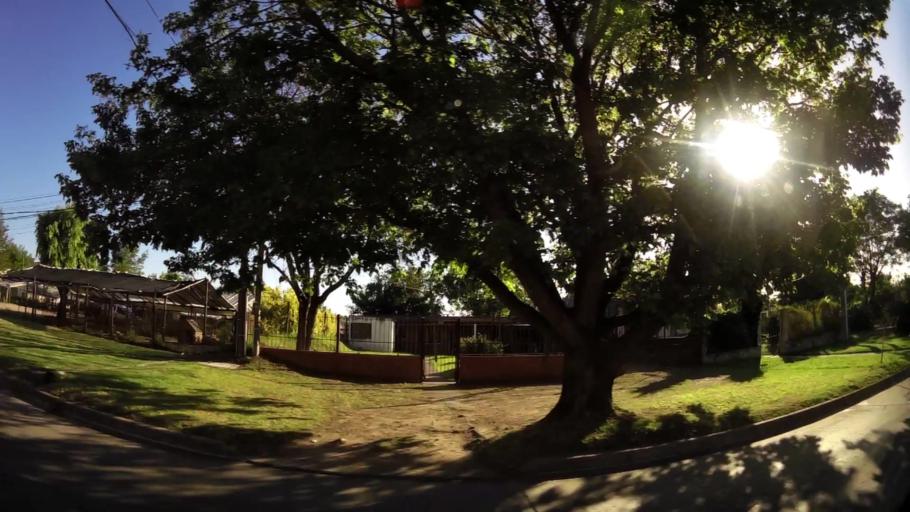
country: UY
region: Montevideo
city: Montevideo
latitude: -34.8401
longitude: -56.2270
